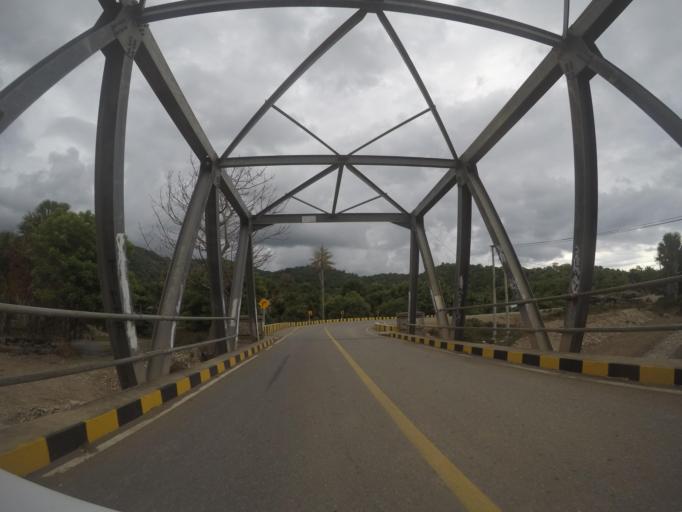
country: TL
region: Liquica
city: Maubara
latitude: -8.7956
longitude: 125.1012
